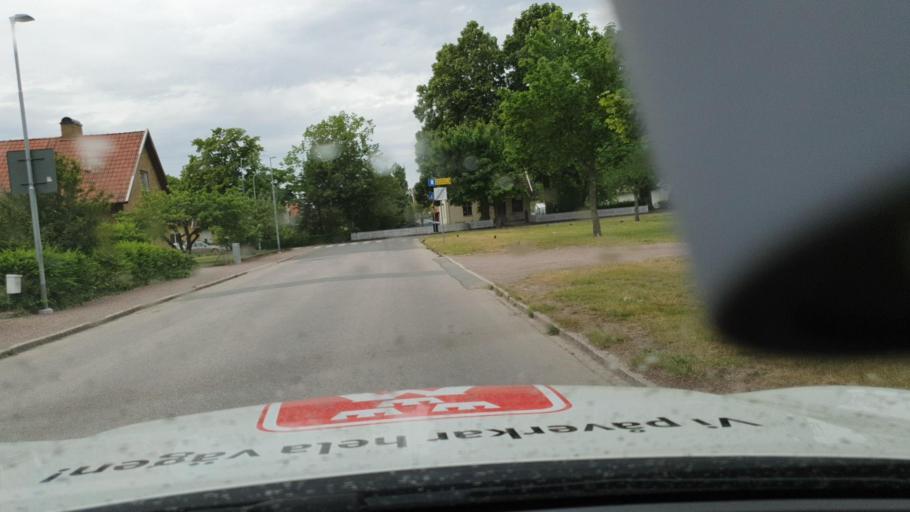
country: SE
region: Vaestra Goetaland
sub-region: Hjo Kommun
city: Hjo
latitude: 58.3091
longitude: 14.2910
